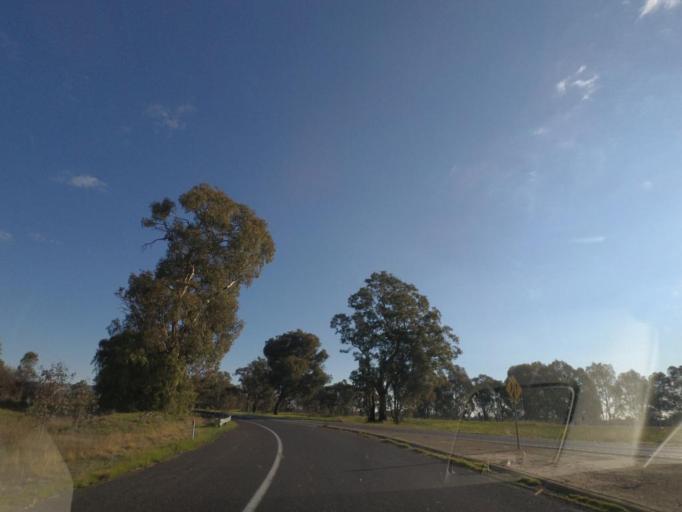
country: AU
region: Victoria
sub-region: Benalla
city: Benalla
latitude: -36.6965
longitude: 145.6574
